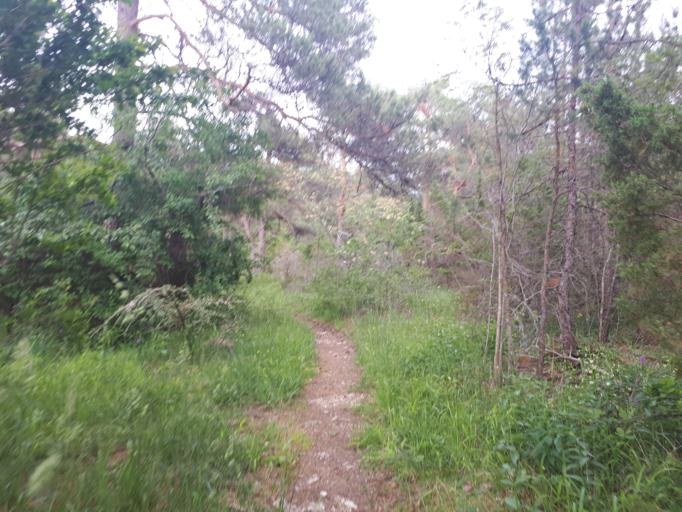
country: SE
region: Gotland
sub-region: Gotland
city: Visby
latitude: 57.6008
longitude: 18.3048
